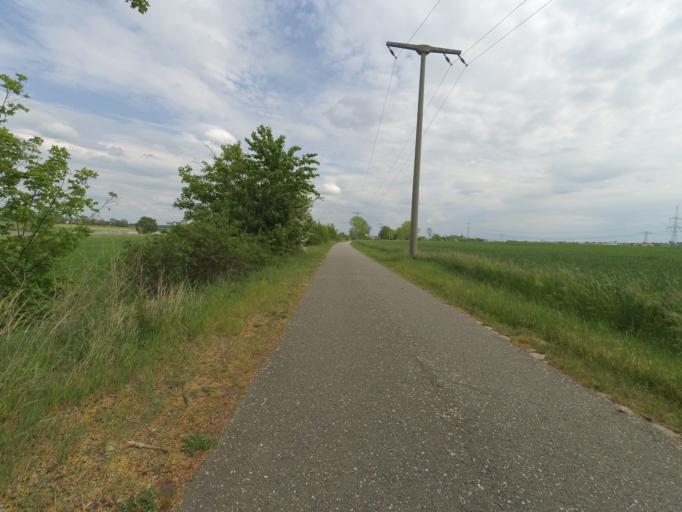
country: DE
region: Saxony
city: Strehla
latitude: 51.3467
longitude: 13.2544
